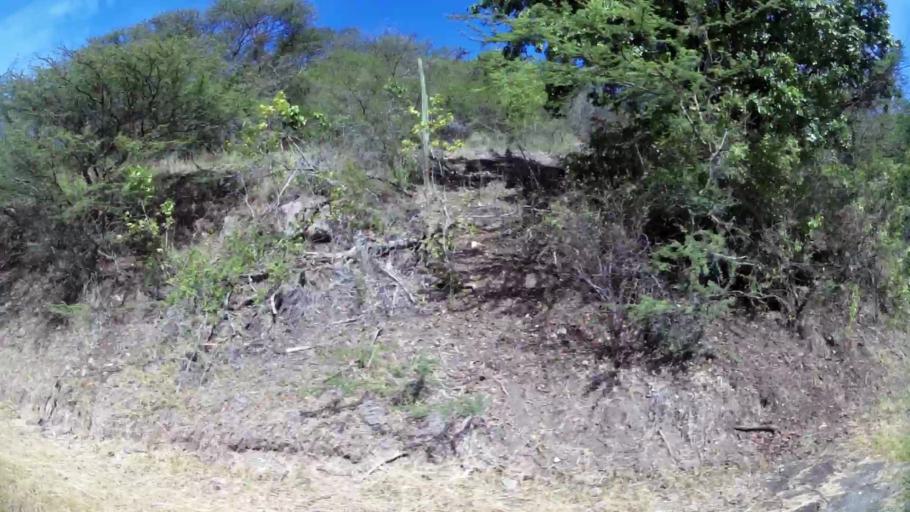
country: AG
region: Saint Paul
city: Falmouth
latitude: 17.0193
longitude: -61.7394
